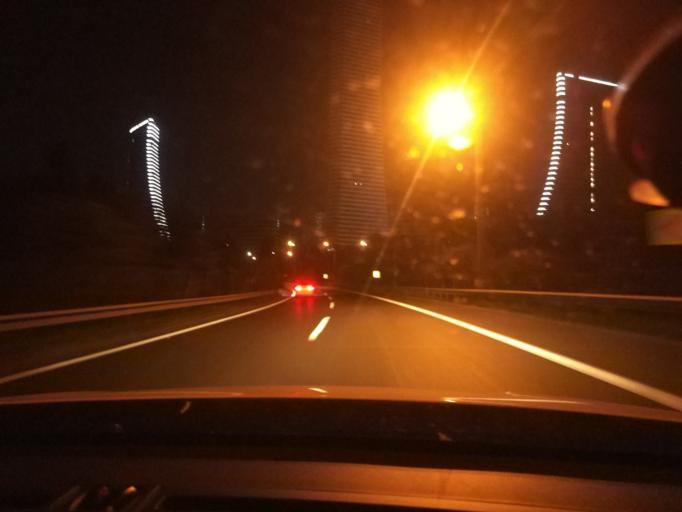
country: TR
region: Istanbul
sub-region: Atasehir
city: Atasehir
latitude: 40.9984
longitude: 29.1194
